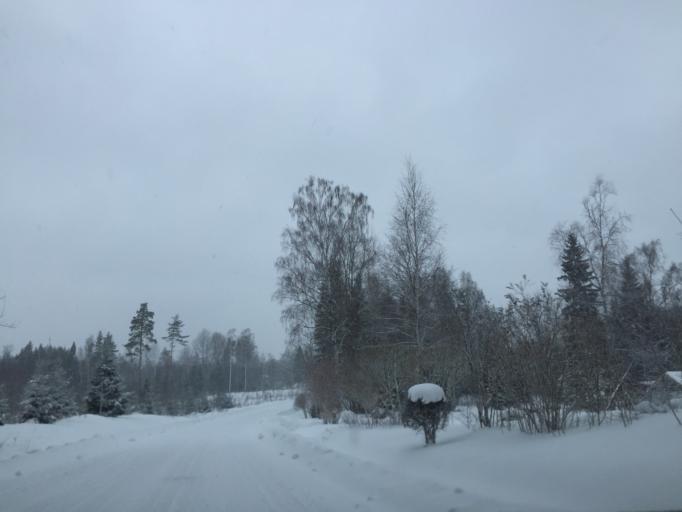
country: LV
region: Amatas Novads
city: Drabesi
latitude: 57.1643
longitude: 25.2853
